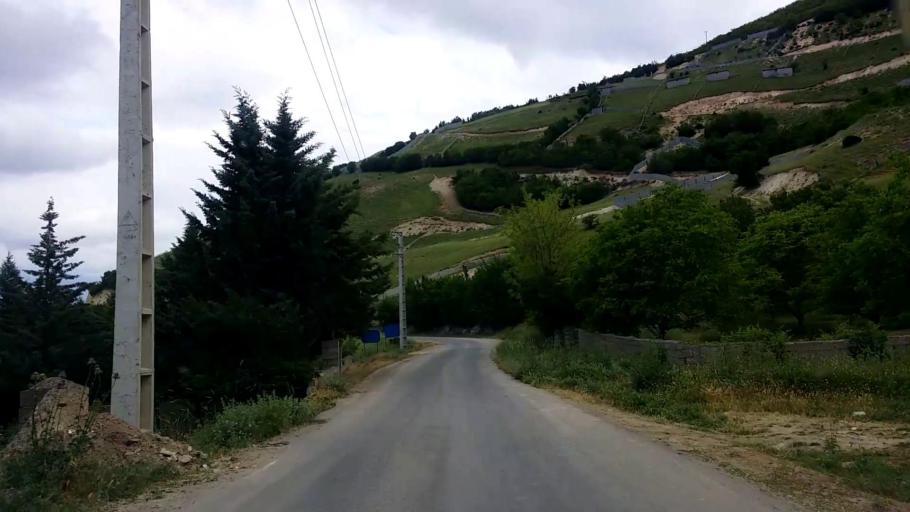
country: IR
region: Mazandaran
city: Chalus
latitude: 36.5452
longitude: 51.2712
